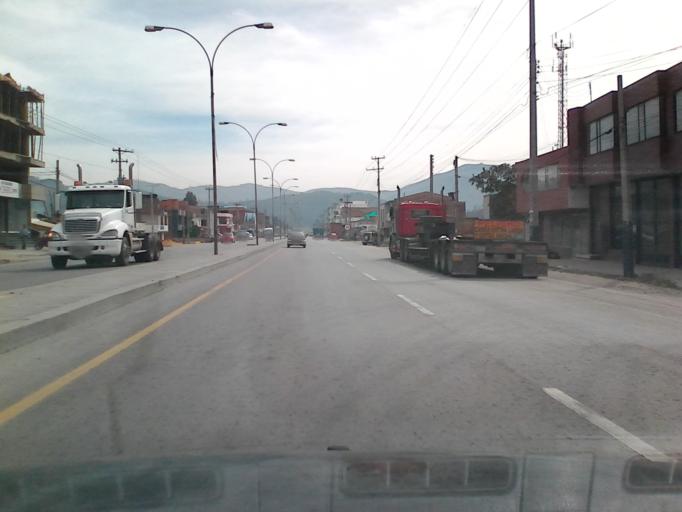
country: CO
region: Boyaca
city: Duitama
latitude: 5.8077
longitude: -73.0247
